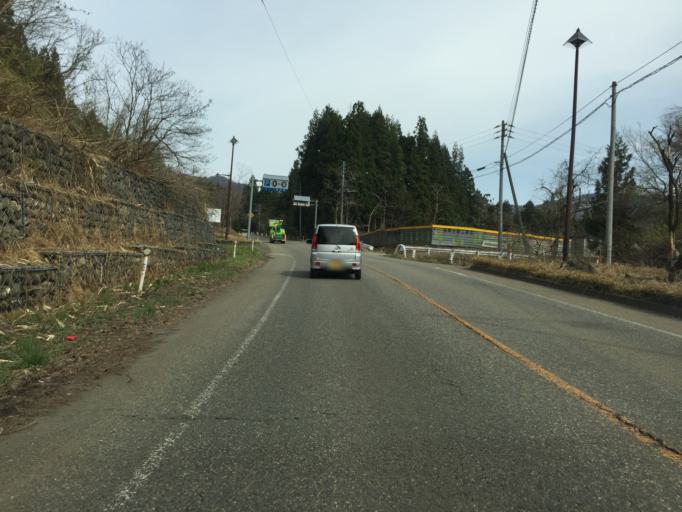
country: JP
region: Niigata
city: Nagaoka
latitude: 37.4525
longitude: 138.9035
